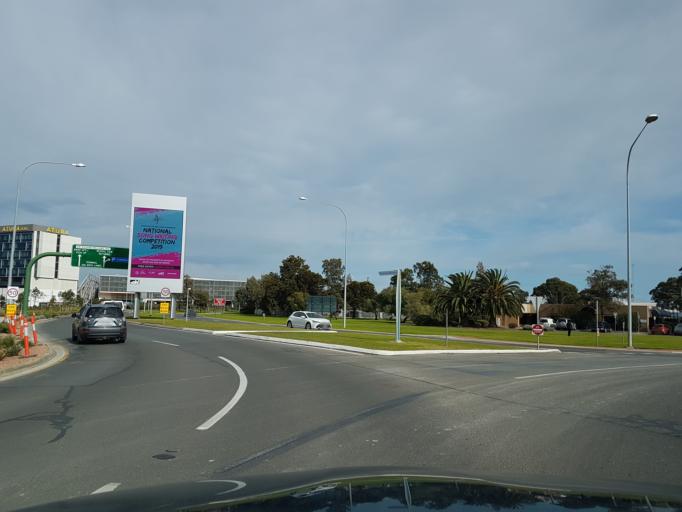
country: AU
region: South Australia
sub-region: City of West Torrens
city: Plympton
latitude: -34.9357
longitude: 138.5396
